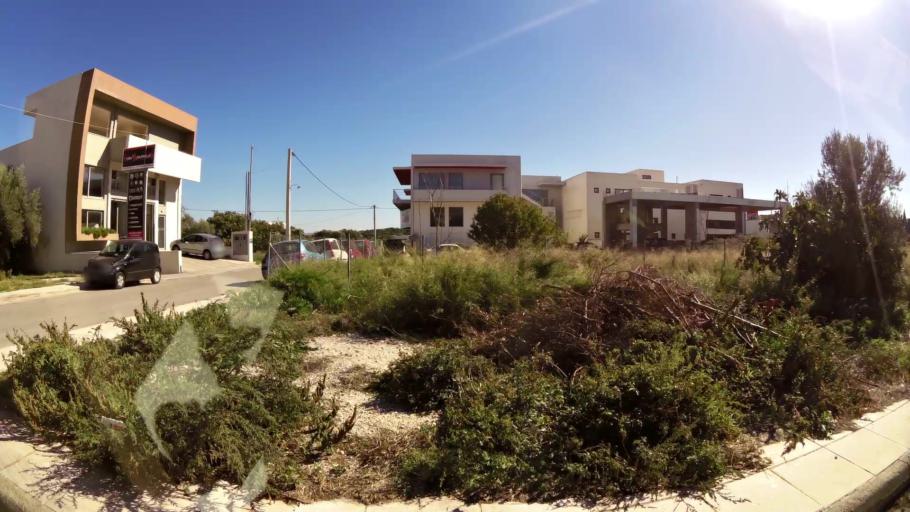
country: GR
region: Attica
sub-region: Nomarchia Anatolikis Attikis
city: Koropi
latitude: 37.8968
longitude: 23.8805
